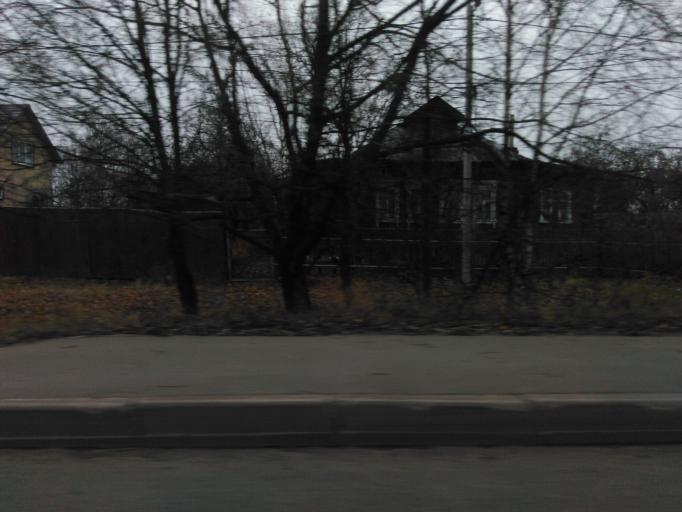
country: RU
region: Moskovskaya
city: Sofrino
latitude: 56.1169
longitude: 37.9614
